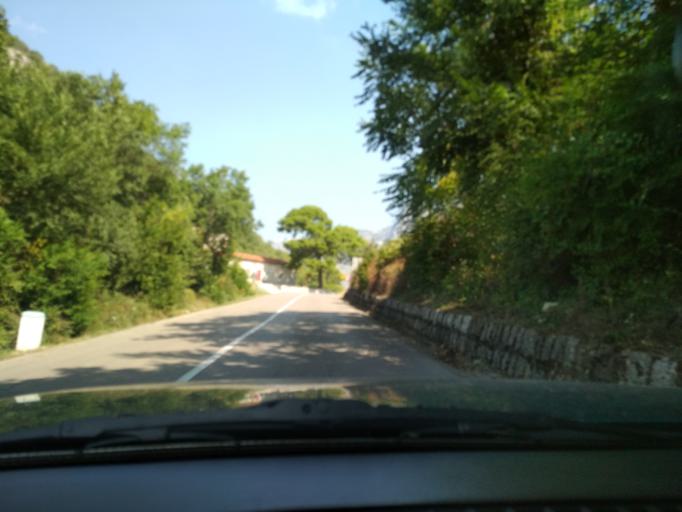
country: ME
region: Kotor
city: Kotor
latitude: 42.4021
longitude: 18.7623
